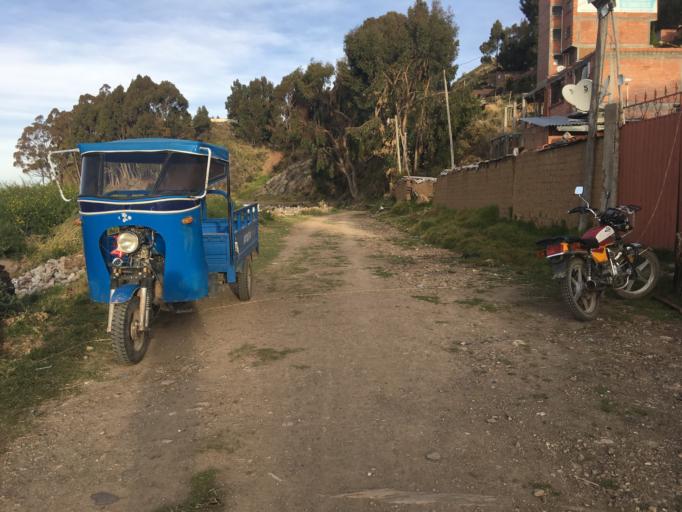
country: BO
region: La Paz
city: San Pedro
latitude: -16.2239
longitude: -68.8506
